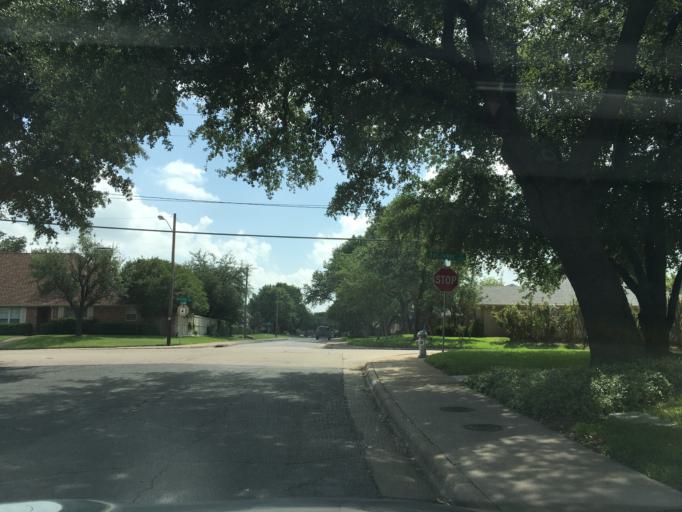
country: US
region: Texas
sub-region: Dallas County
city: University Park
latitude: 32.8923
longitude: -96.7779
